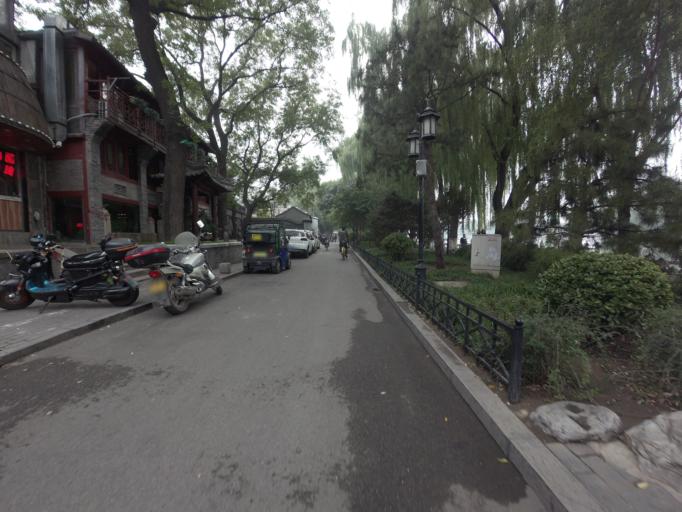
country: CN
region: Beijing
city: Jingshan
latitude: 39.9344
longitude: 116.3885
